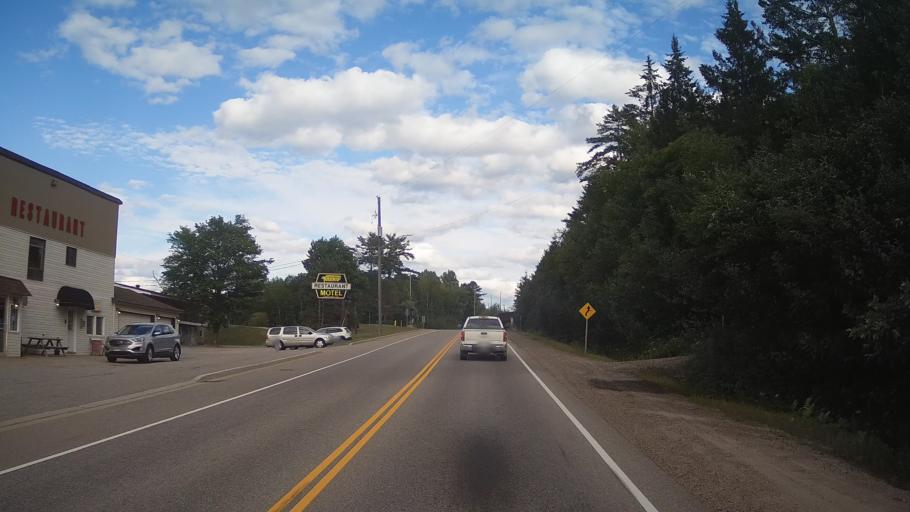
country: CA
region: Ontario
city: Mattawa
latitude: 46.3158
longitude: -78.6924
